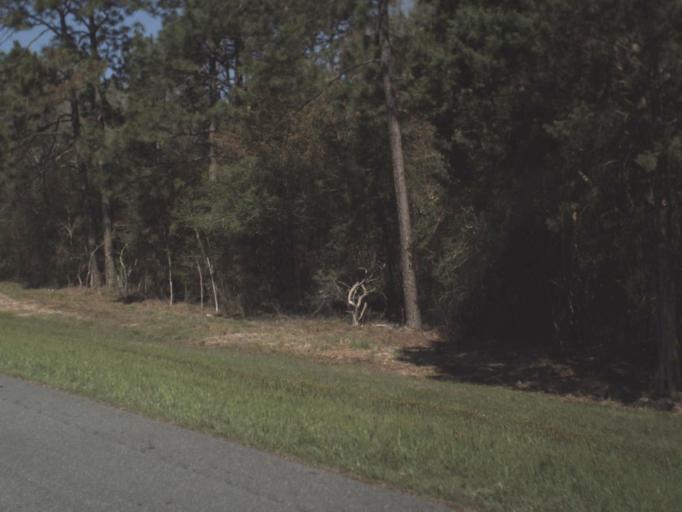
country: US
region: Florida
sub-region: Walton County
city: DeFuniak Springs
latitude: 30.6910
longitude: -86.0540
